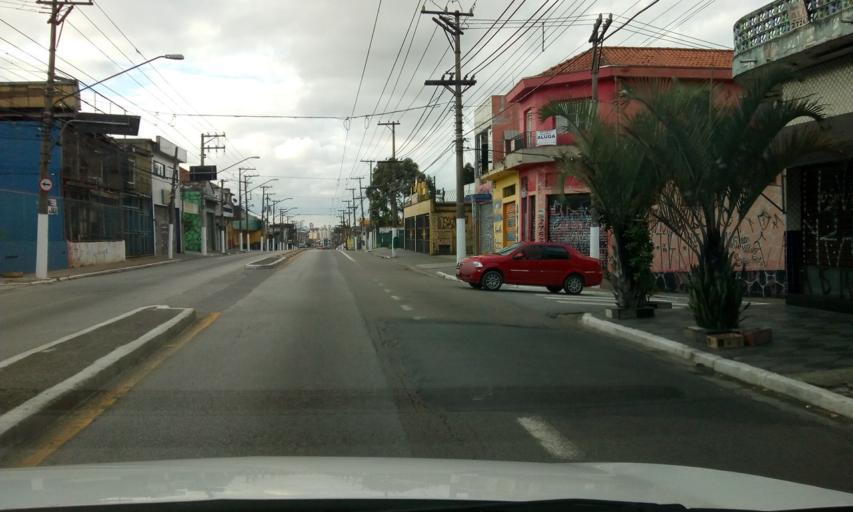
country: BR
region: Sao Paulo
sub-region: Sao Caetano Do Sul
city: Sao Caetano do Sul
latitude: -23.5772
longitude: -46.5034
